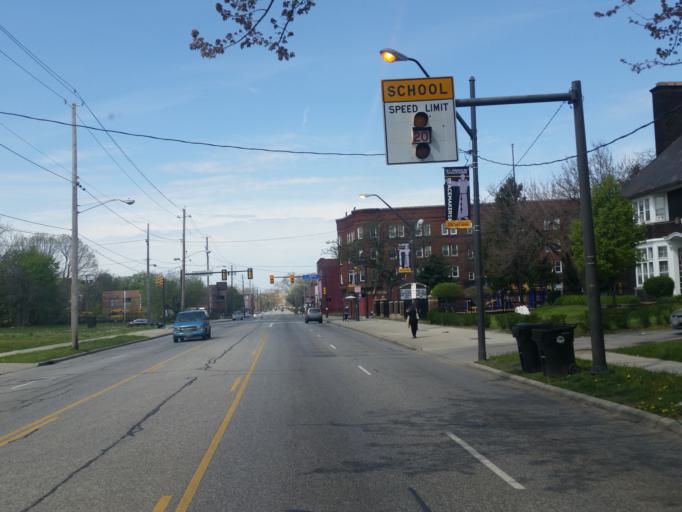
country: US
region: Ohio
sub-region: Cuyahoga County
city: Bratenahl
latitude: 41.5194
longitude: -81.6384
